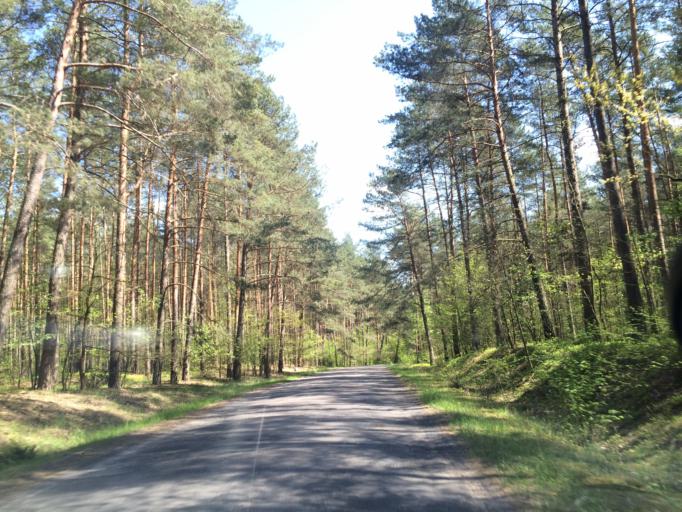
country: PL
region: Warmian-Masurian Voivodeship
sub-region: Powiat nowomiejski
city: Kurzetnik
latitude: 53.3710
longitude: 19.5082
